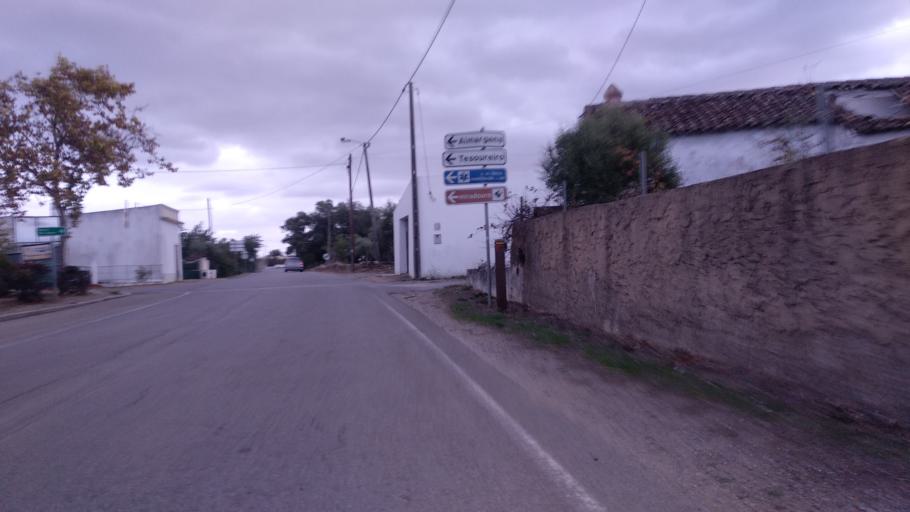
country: PT
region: Faro
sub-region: Sao Bras de Alportel
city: Sao Bras de Alportel
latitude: 37.1682
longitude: -7.9067
